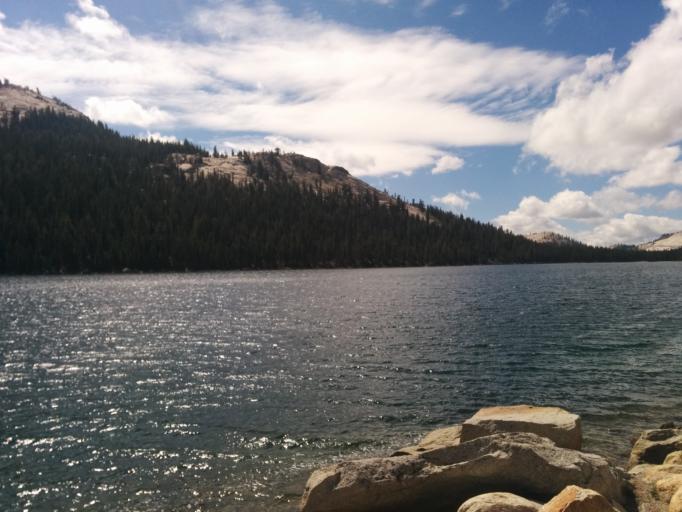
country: US
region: California
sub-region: Mariposa County
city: Yosemite Valley
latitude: 37.8346
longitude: -119.4575
